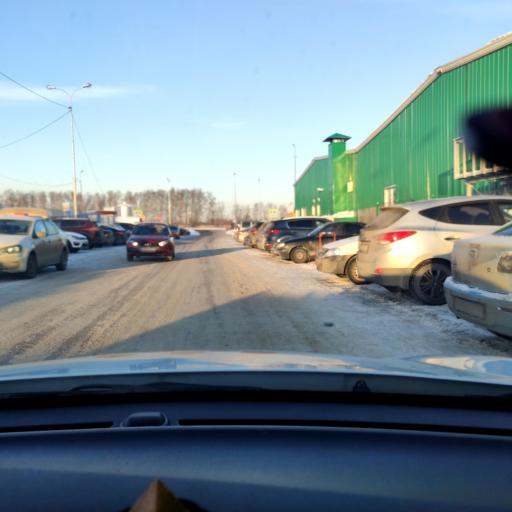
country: RU
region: Tatarstan
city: Osinovo
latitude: 55.8574
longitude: 48.8334
